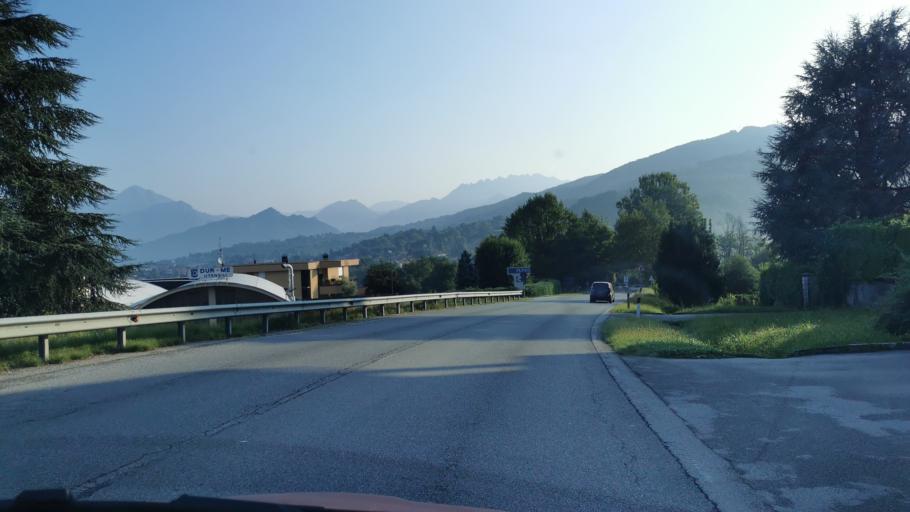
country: IT
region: Lombardy
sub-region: Provincia di Lecco
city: Cologna-Caraverio
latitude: 45.7536
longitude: 9.3336
